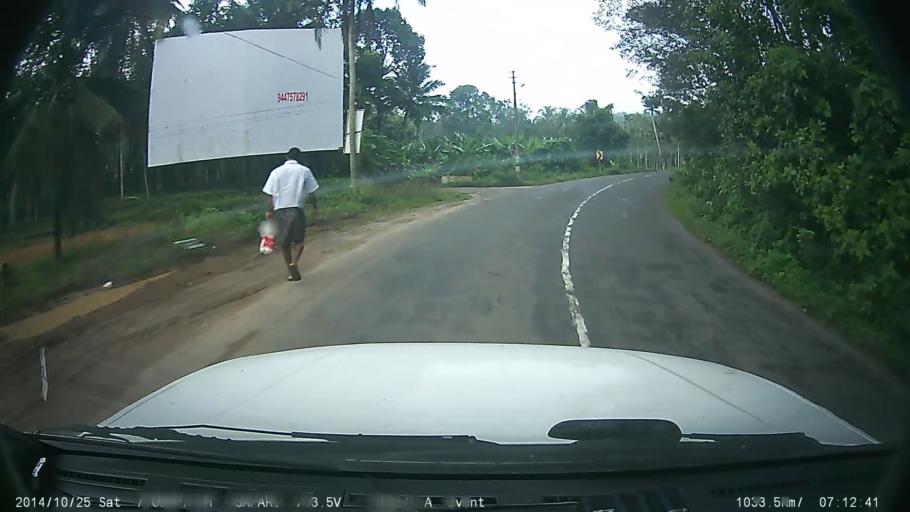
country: IN
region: Kerala
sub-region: Kottayam
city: Palackattumala
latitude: 9.8281
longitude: 76.5911
